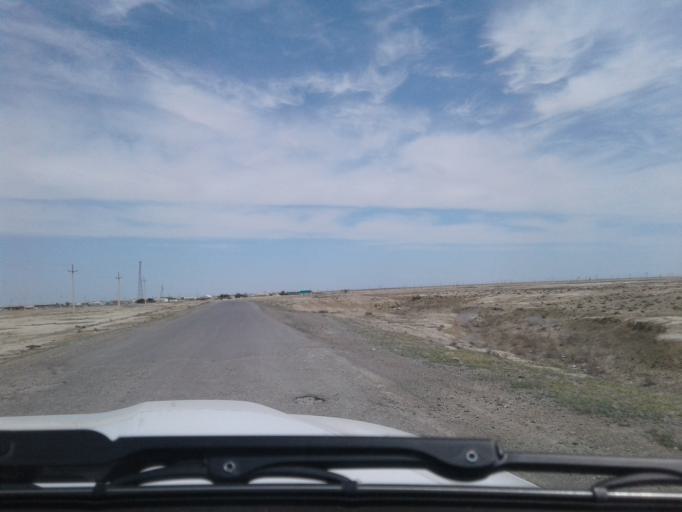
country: TM
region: Balkan
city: Gazanjyk
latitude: 39.2024
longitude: 55.7091
